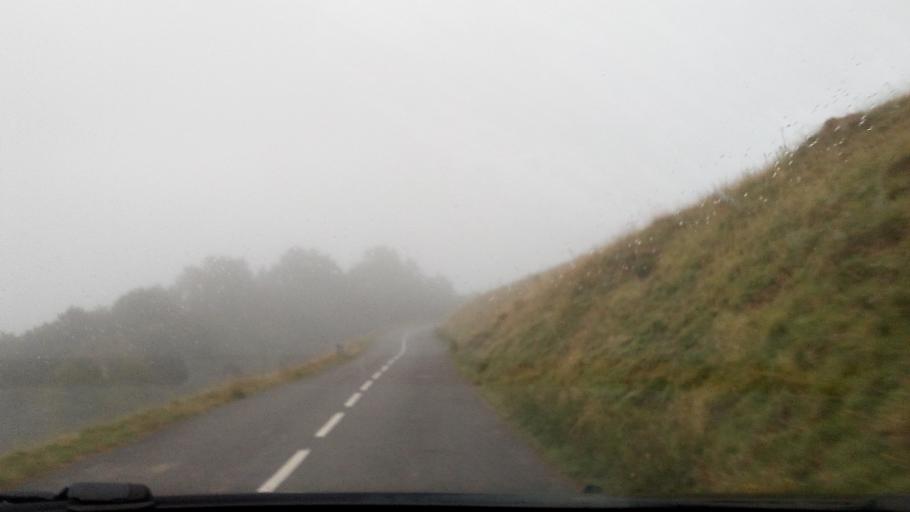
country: FR
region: Aquitaine
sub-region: Departement des Pyrenees-Atlantiques
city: Laruns
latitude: 42.9747
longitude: -0.3070
